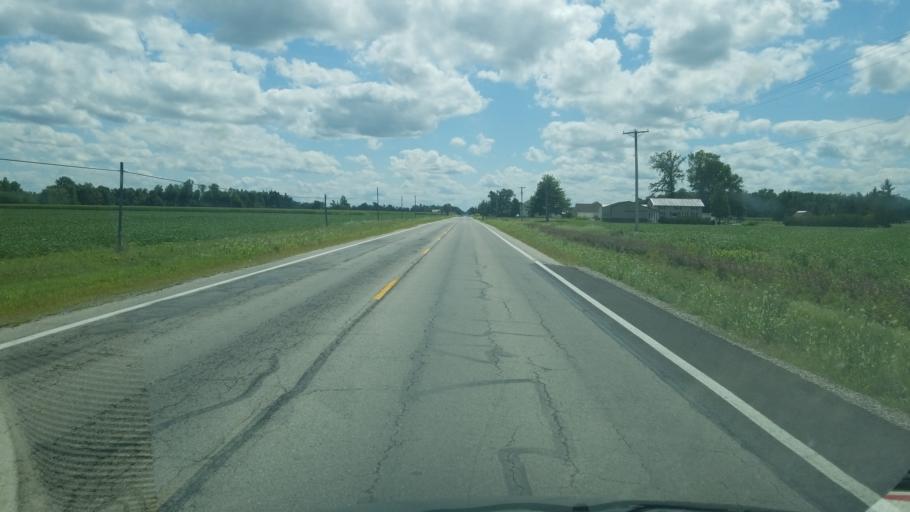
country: US
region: Ohio
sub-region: Henry County
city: Napoleon
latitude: 41.3247
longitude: -84.1186
